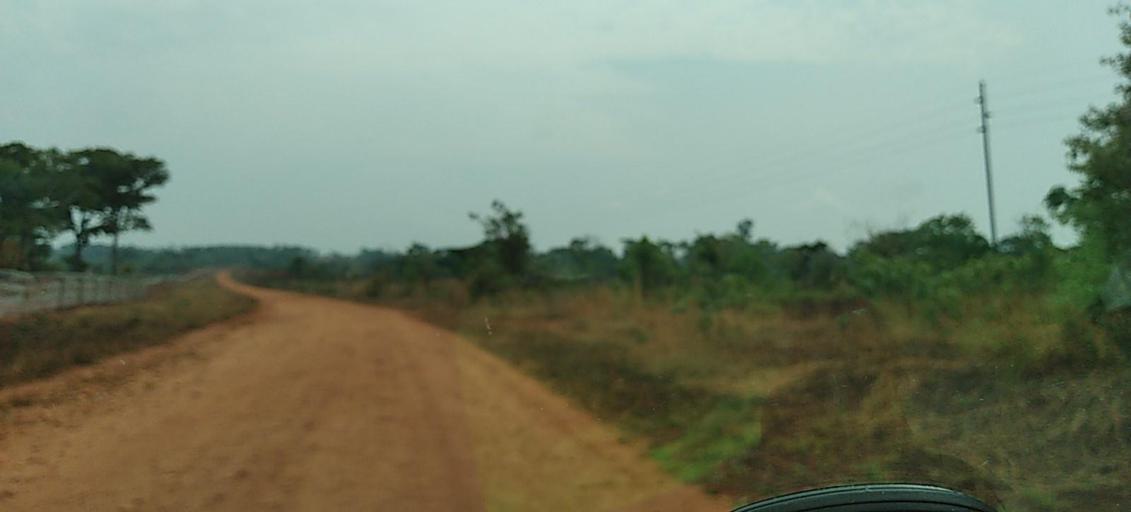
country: ZM
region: North-Western
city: Kansanshi
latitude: -12.1078
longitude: 26.4904
